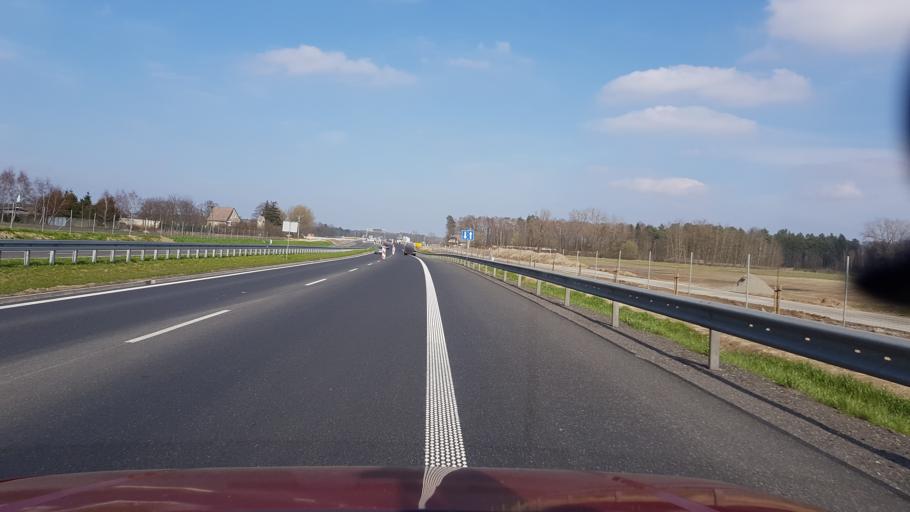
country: PL
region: West Pomeranian Voivodeship
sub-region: Powiat goleniowski
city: Nowogard
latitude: 53.6462
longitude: 15.0690
